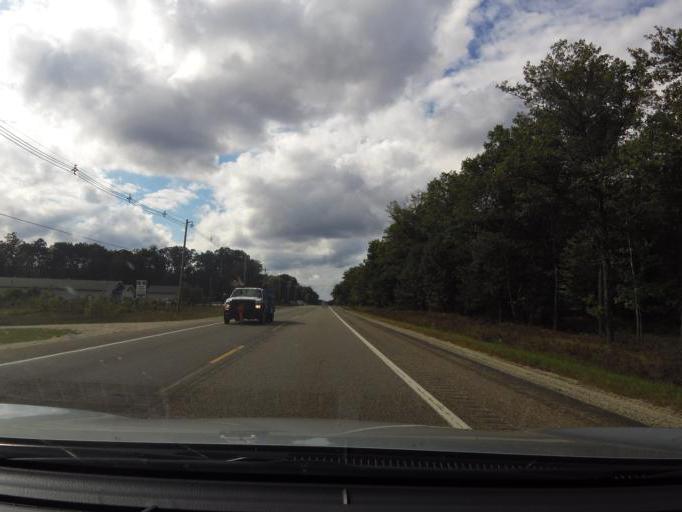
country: US
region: Michigan
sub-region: Roscommon County
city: Prudenville
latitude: 44.3054
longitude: -84.6145
